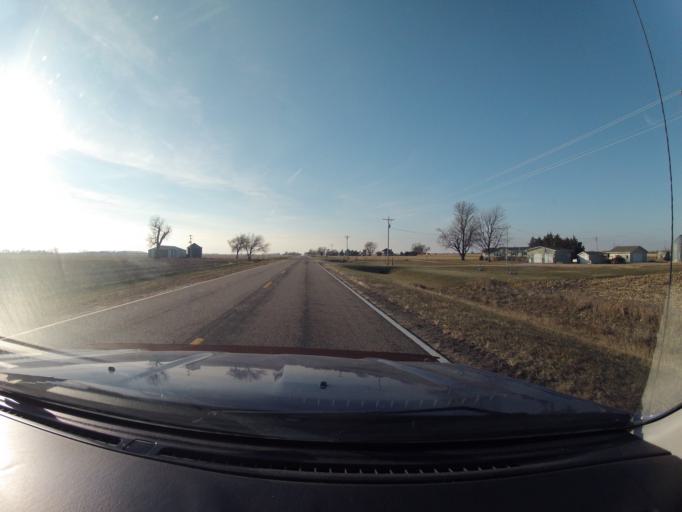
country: US
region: Nebraska
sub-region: Buffalo County
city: Kearney
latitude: 40.6410
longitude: -98.9688
